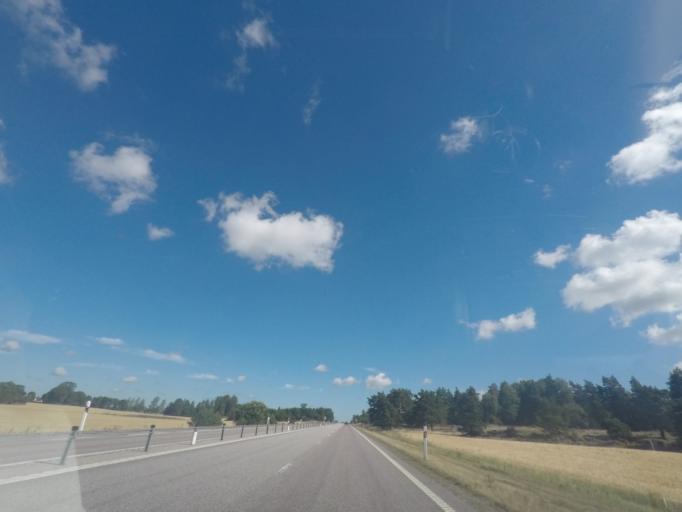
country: SE
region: Uppsala
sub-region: Enkopings Kommun
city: Grillby
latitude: 59.6664
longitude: 17.2682
